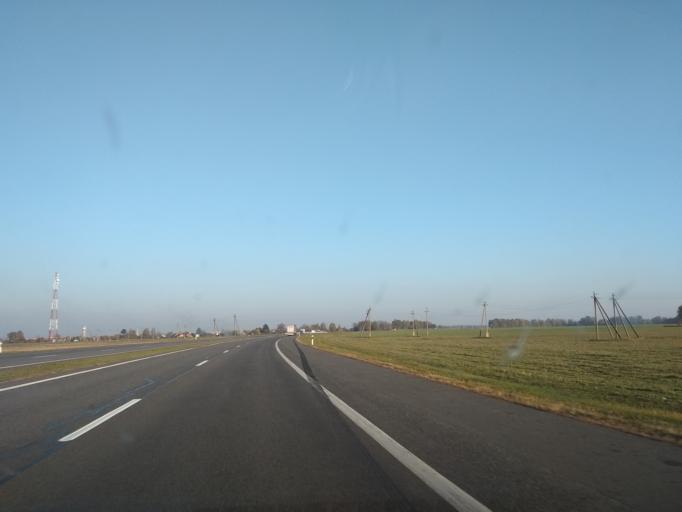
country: BY
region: Brest
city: Kobryn
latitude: 52.1995
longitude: 24.2900
